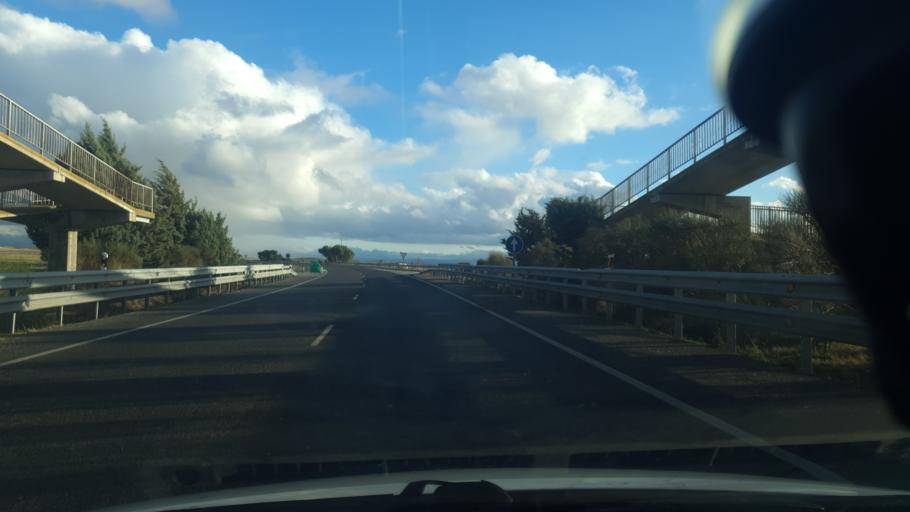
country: ES
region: Castille and Leon
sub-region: Provincia de Segovia
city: Codorniz
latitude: 41.0549
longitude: -4.6291
